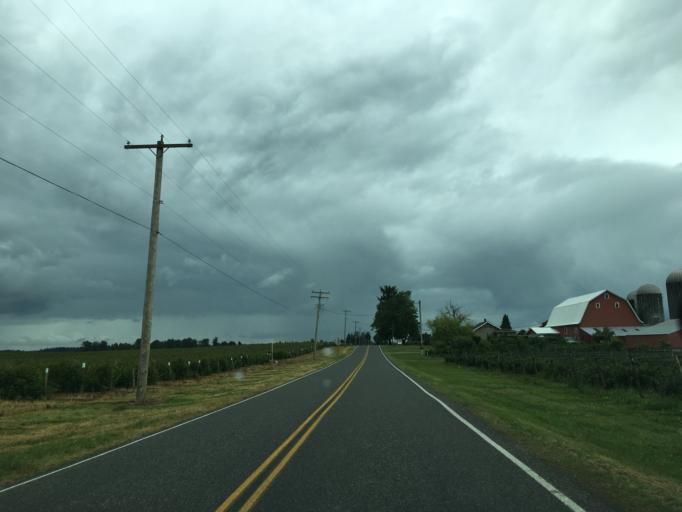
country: US
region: Washington
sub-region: Whatcom County
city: Nooksack
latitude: 48.9819
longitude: -122.3520
